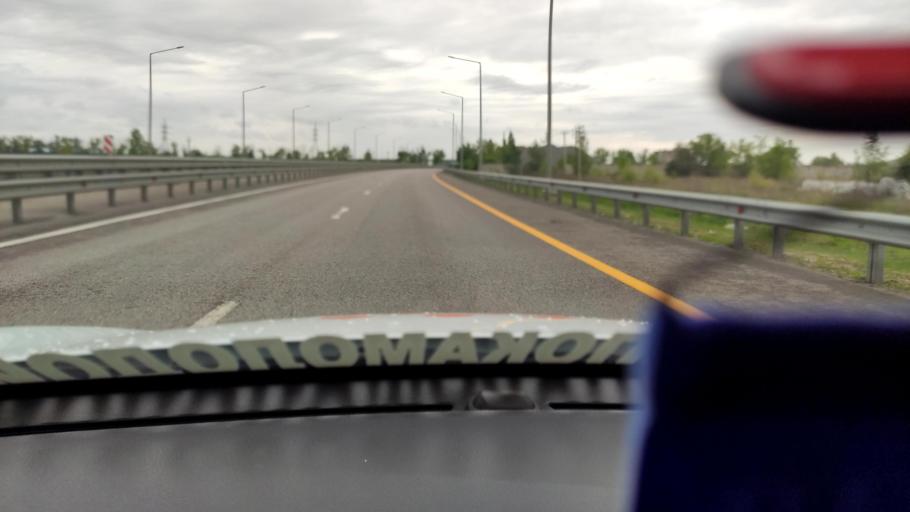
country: RU
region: Voronezj
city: Novaya Usman'
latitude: 51.6326
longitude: 39.3178
